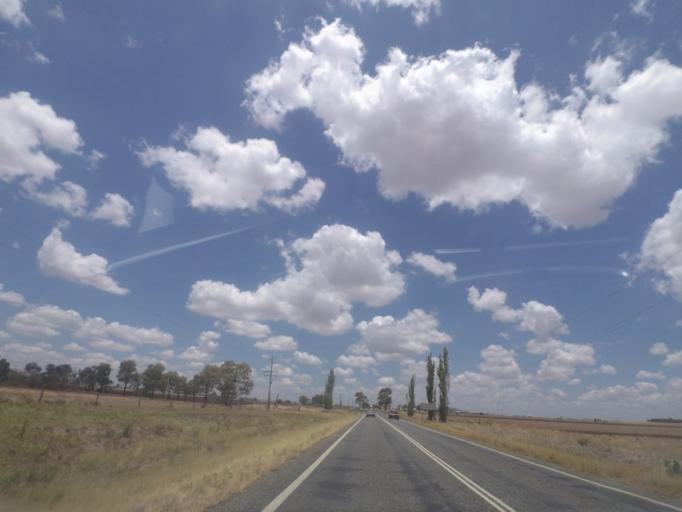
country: AU
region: Queensland
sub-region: Toowoomba
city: Top Camp
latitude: -27.9253
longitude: 151.9842
